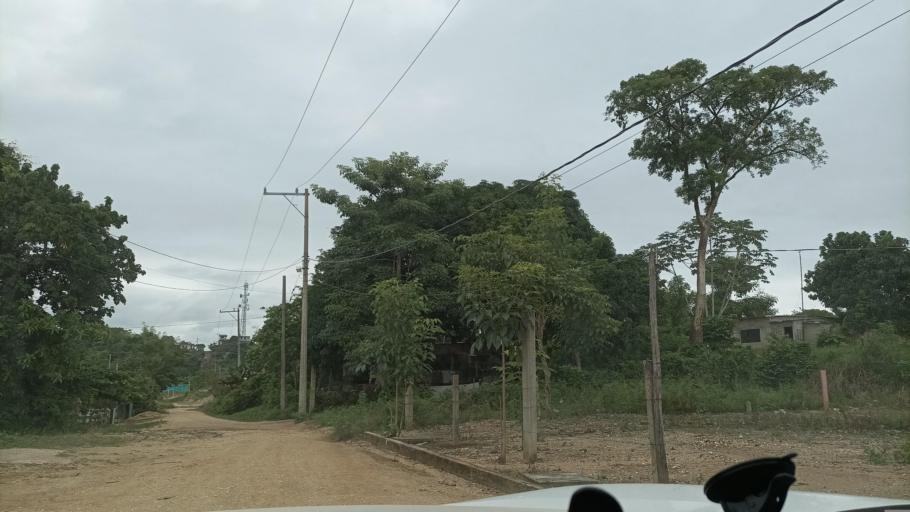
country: MX
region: Veracruz
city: Hidalgotitlan
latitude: 17.7704
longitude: -94.6531
